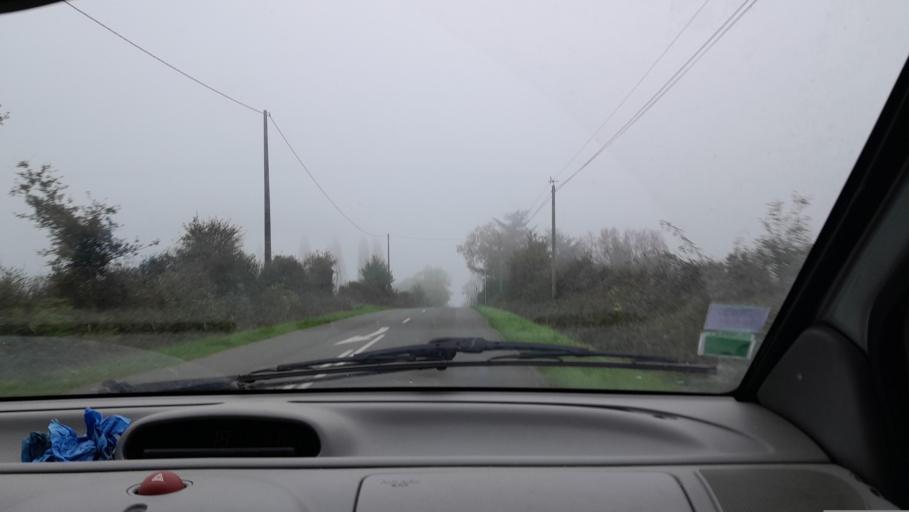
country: FR
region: Pays de la Loire
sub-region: Departement de la Mayenne
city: Ahuille
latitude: 48.0373
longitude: -0.8949
